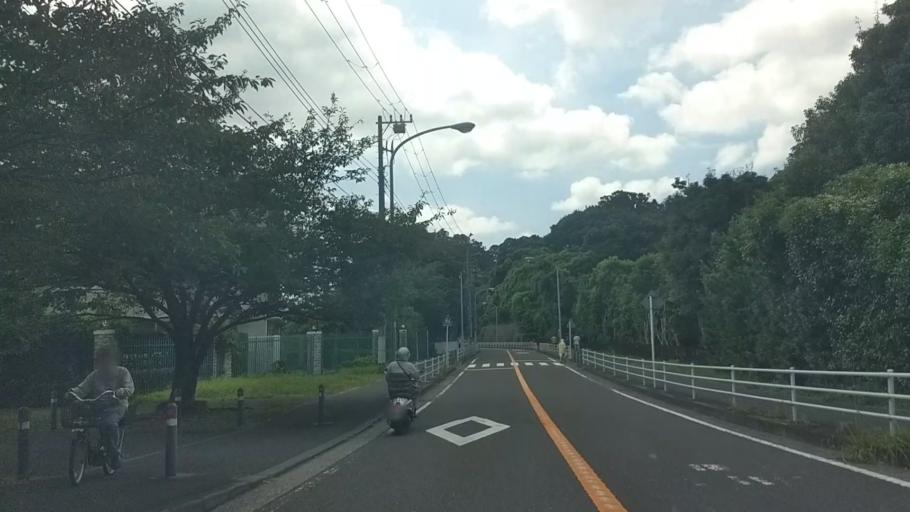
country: JP
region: Kanagawa
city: Yokosuka
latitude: 35.3593
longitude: 139.6358
